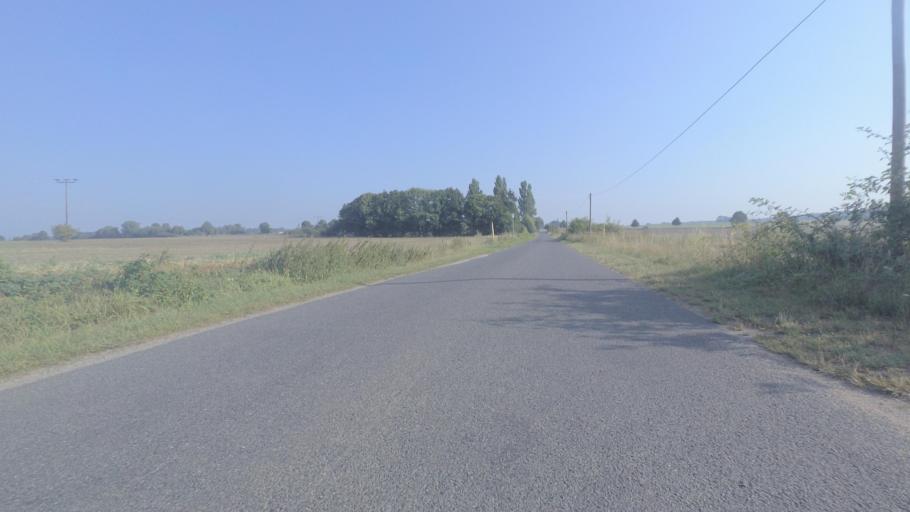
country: DE
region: Mecklenburg-Vorpommern
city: Malchow
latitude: 53.3628
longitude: 12.3816
